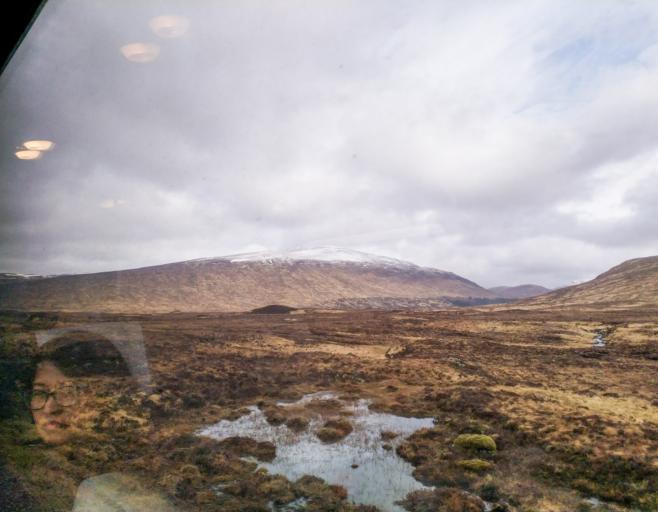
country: GB
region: Scotland
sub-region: Highland
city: Spean Bridge
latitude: 56.7491
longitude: -4.6748
